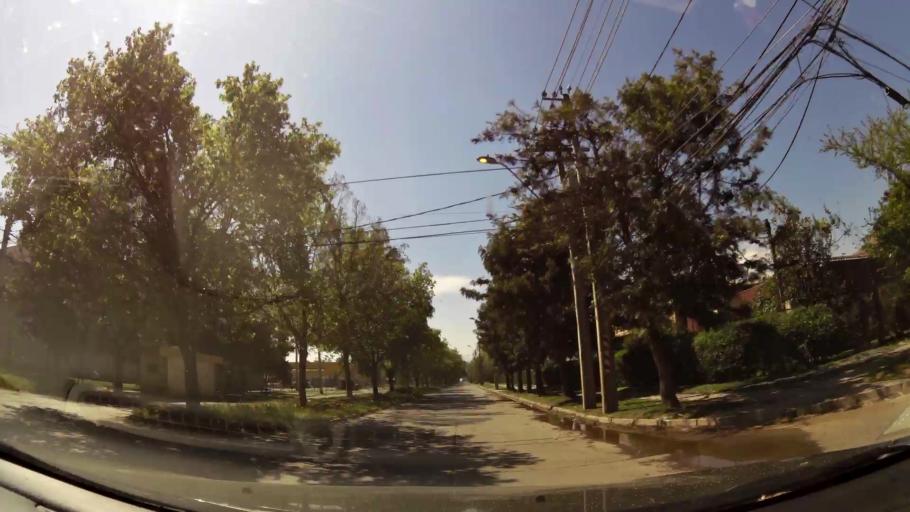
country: CL
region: Santiago Metropolitan
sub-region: Provincia de Santiago
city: Lo Prado
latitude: -33.3839
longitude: -70.7480
